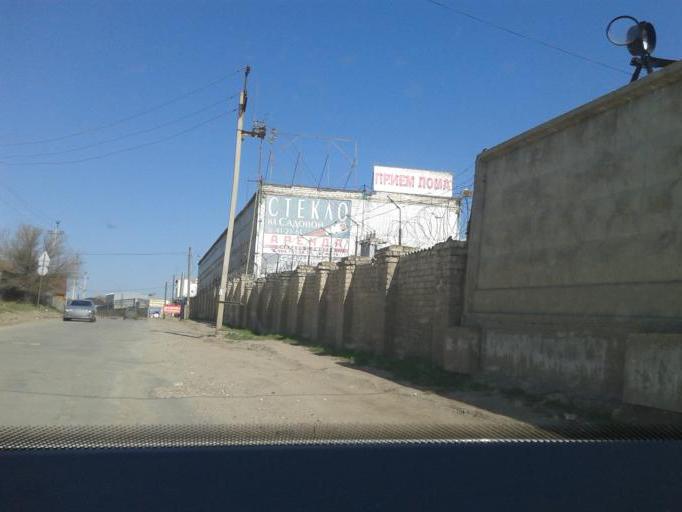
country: RU
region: Volgograd
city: Volgograd
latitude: 48.6799
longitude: 44.4624
